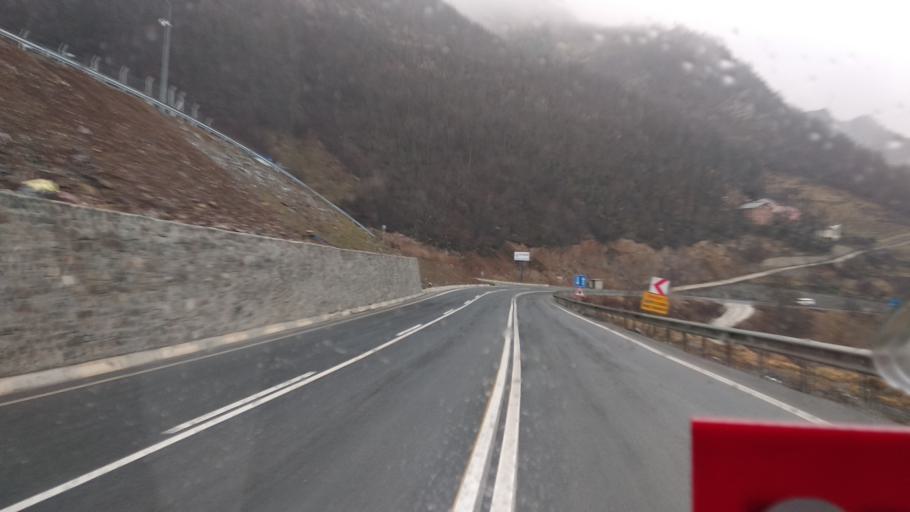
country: TR
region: Trabzon
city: Macka
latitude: 40.7162
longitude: 39.5147
